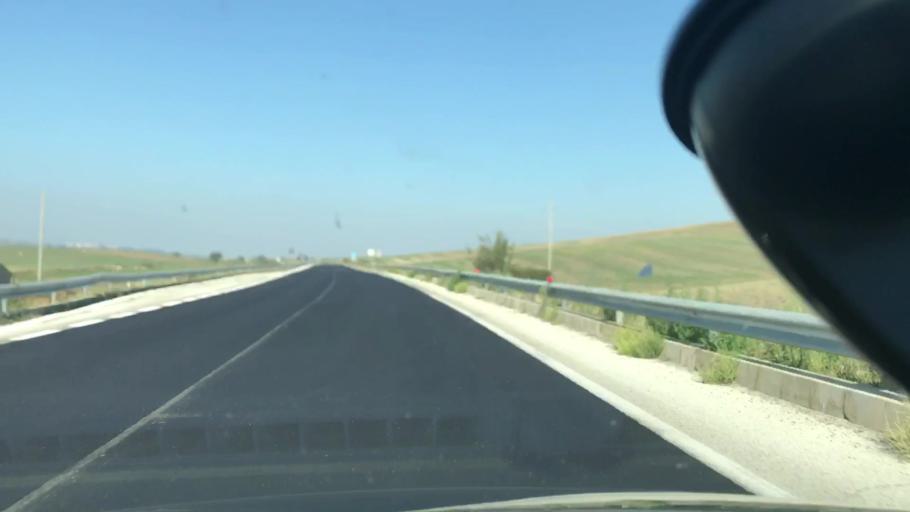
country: IT
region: Apulia
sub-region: Provincia di Barletta - Andria - Trani
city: Spinazzola
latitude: 40.9212
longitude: 16.0953
